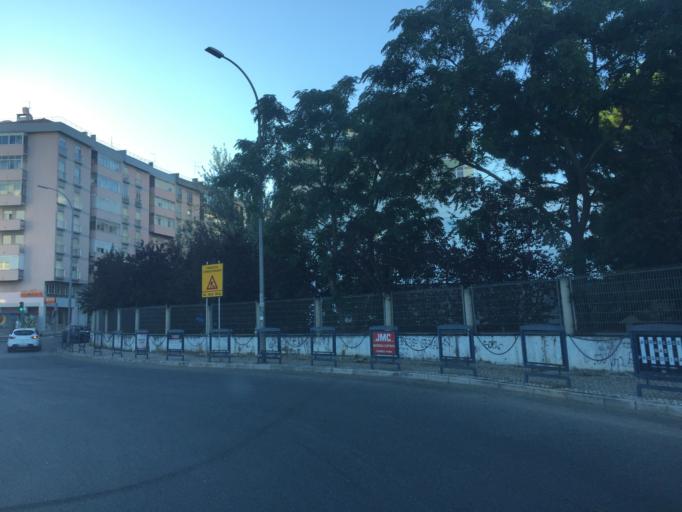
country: PT
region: Lisbon
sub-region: Odivelas
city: Olival do Basto
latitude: 38.7895
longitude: -9.1744
